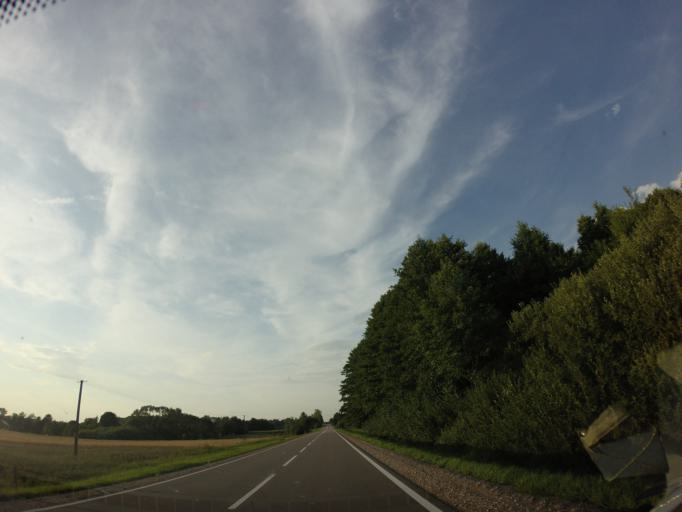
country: LT
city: Lazdijai
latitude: 54.1399
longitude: 23.4663
